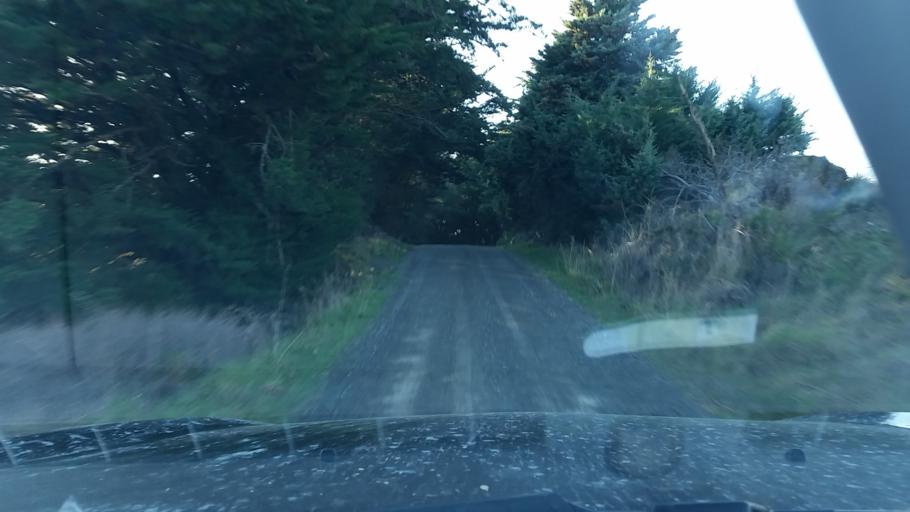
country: NZ
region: Marlborough
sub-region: Marlborough District
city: Blenheim
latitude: -41.7355
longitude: 173.9972
